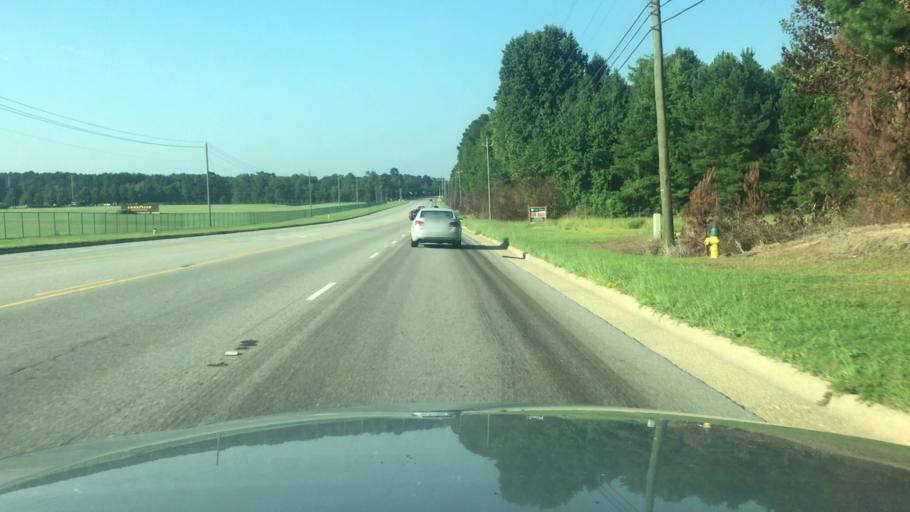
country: US
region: North Carolina
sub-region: Cumberland County
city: Eastover
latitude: 35.1738
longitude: -78.8600
